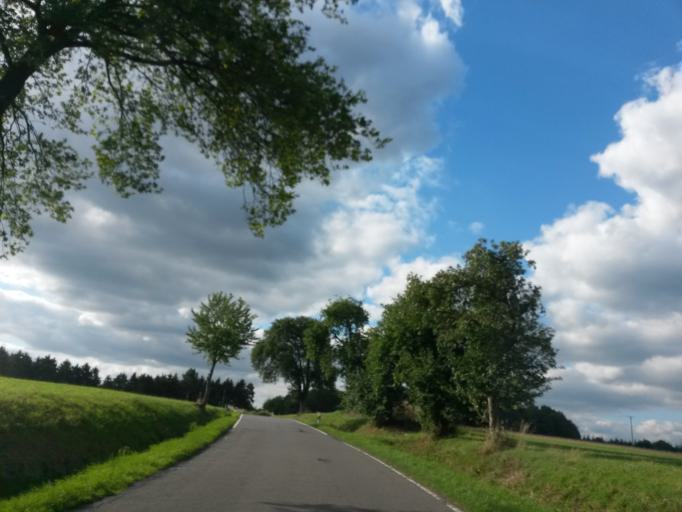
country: DE
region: North Rhine-Westphalia
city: Waldbrol
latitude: 50.9037
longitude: 7.6254
